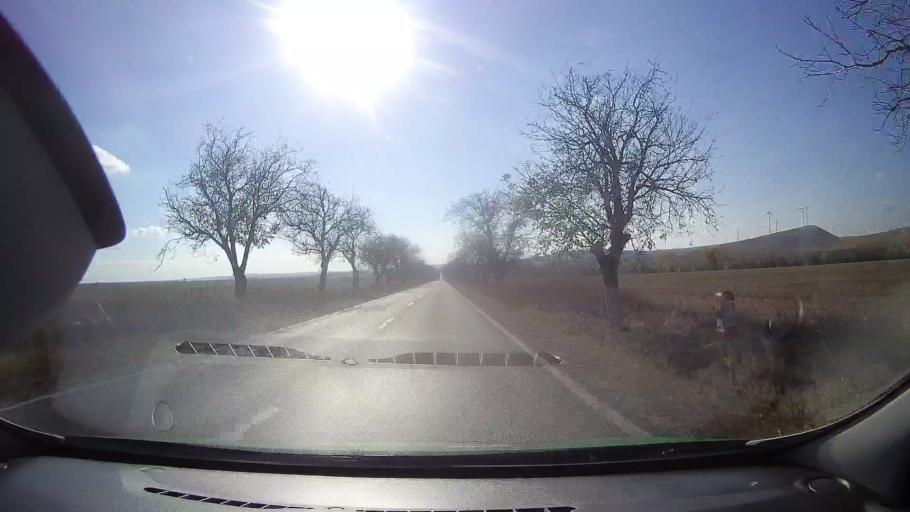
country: RO
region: Tulcea
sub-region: Comuna Ceamurlia de Jos
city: Ceamurlia de Jos
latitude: 44.7816
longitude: 28.6892
